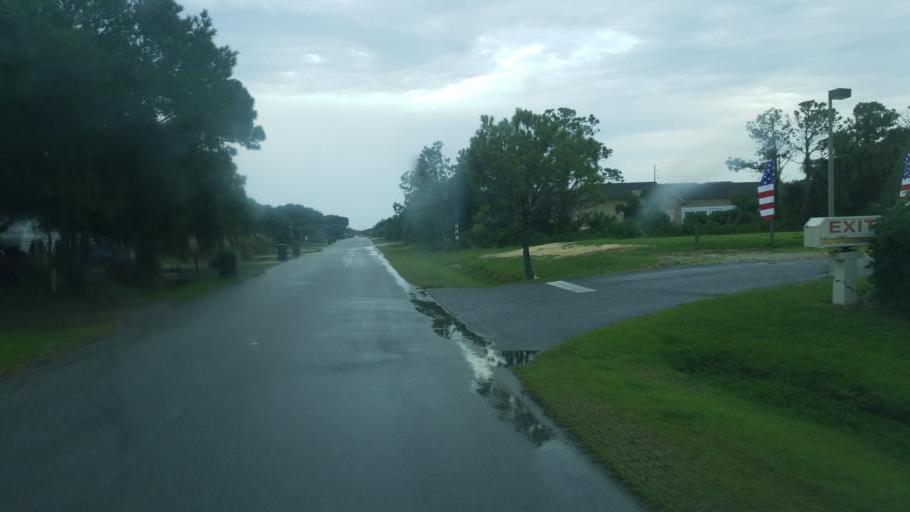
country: US
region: North Carolina
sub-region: Dare County
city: Nags Head
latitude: 35.9867
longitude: -75.6437
